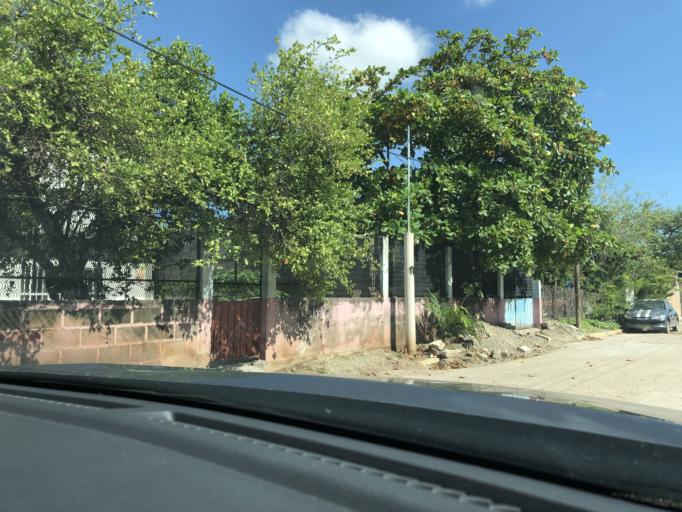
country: MX
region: Oaxaca
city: San Jeronimo Ixtepec
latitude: 16.5584
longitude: -95.1063
